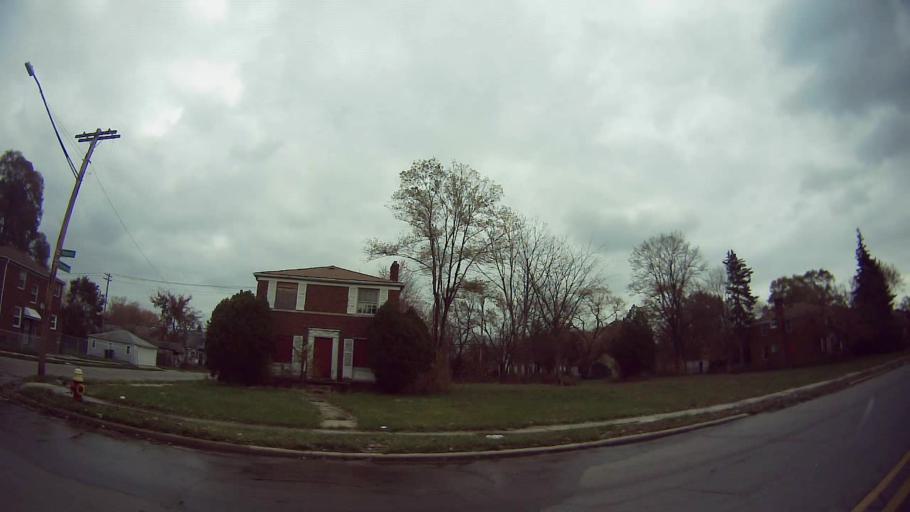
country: US
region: Michigan
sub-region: Macomb County
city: Warren
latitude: 42.4379
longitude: -83.0048
